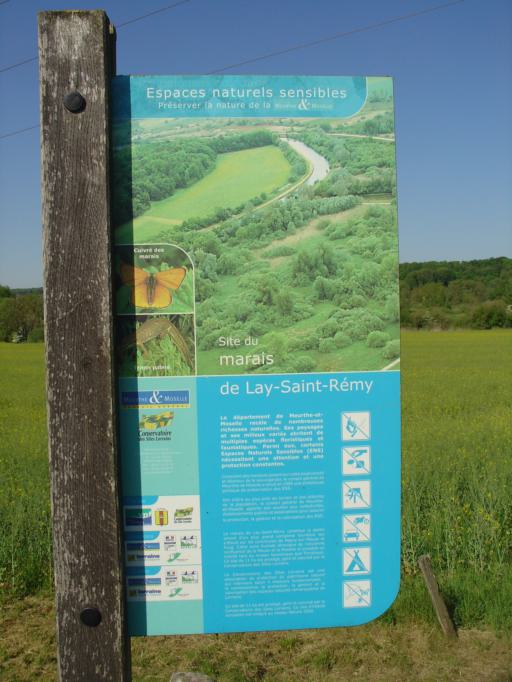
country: FR
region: Lorraine
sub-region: Departement de Meurthe-et-Moselle
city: Foug
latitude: 48.6874
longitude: 5.7657
